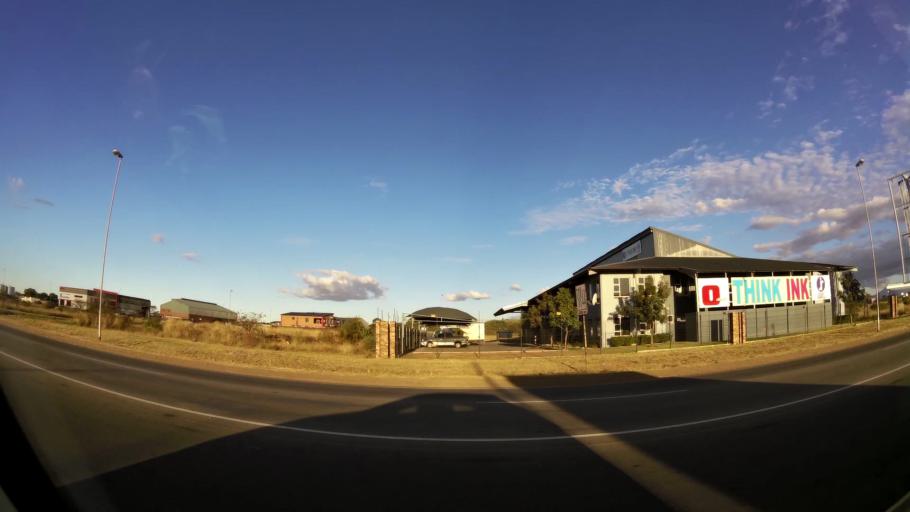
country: ZA
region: Limpopo
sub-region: Capricorn District Municipality
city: Polokwane
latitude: -23.8580
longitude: 29.4728
